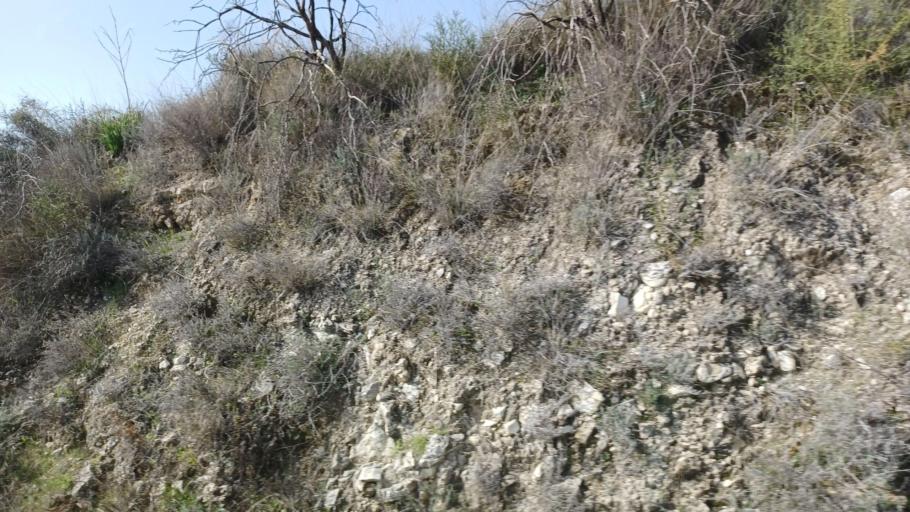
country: CY
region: Limassol
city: Pachna
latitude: 34.7965
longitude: 32.6951
